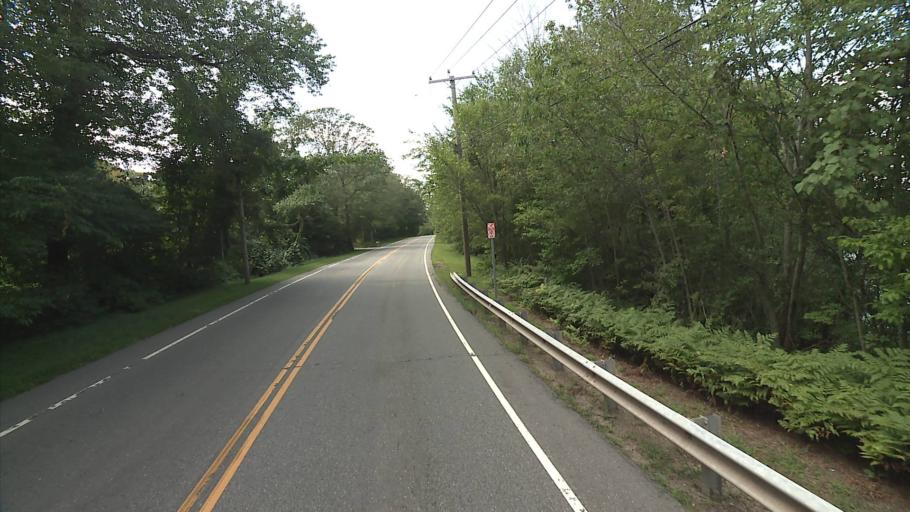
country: US
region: Connecticut
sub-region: New London County
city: Colchester
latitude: 41.6290
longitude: -72.3032
